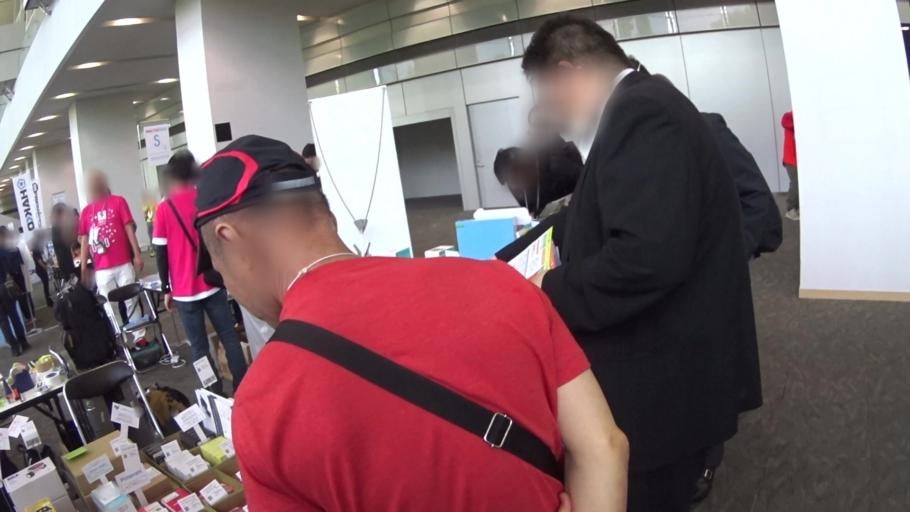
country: JP
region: Nara
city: Nara-shi
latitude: 34.7472
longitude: 135.7806
